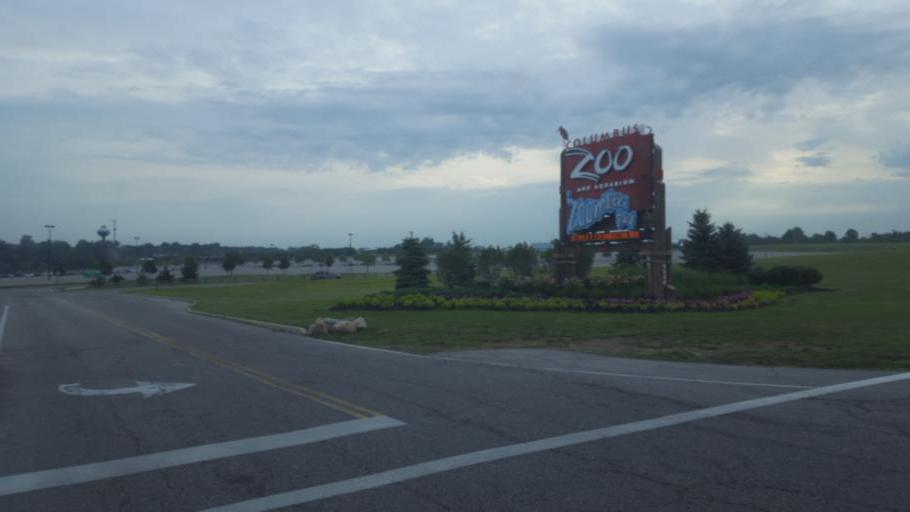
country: US
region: Ohio
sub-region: Delaware County
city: Powell
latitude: 40.1519
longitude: -83.1165
